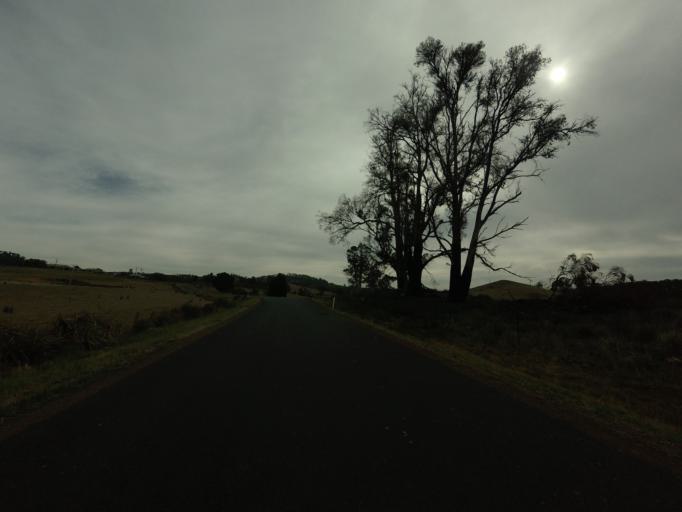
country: AU
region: Tasmania
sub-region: Sorell
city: Sorell
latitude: -42.4562
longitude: 147.5742
